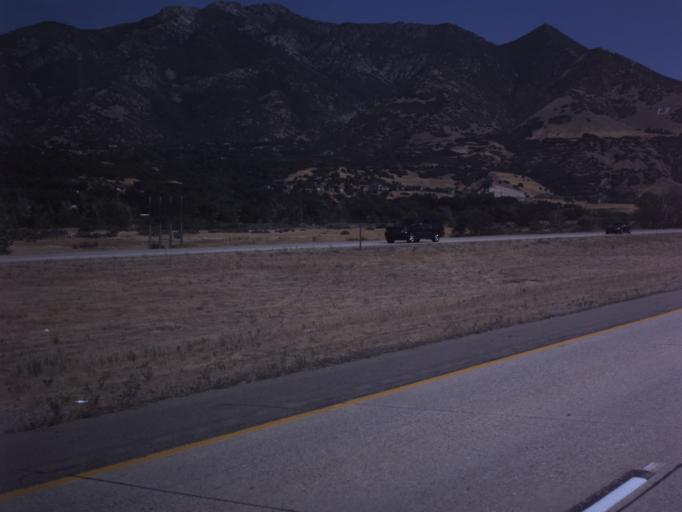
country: US
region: Utah
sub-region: Davis County
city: South Weber
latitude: 41.1363
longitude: -111.9294
